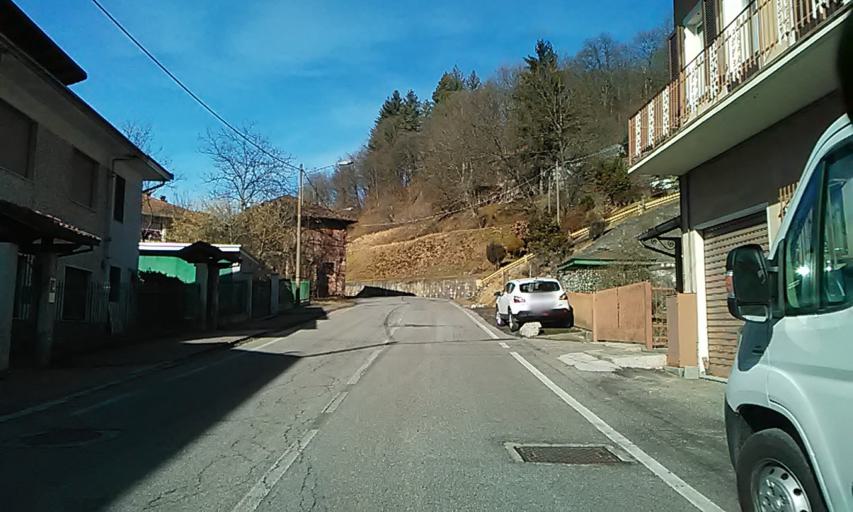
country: IT
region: Piedmont
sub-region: Provincia di Vercelli
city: Valduggia
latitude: 45.7278
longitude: 8.3014
